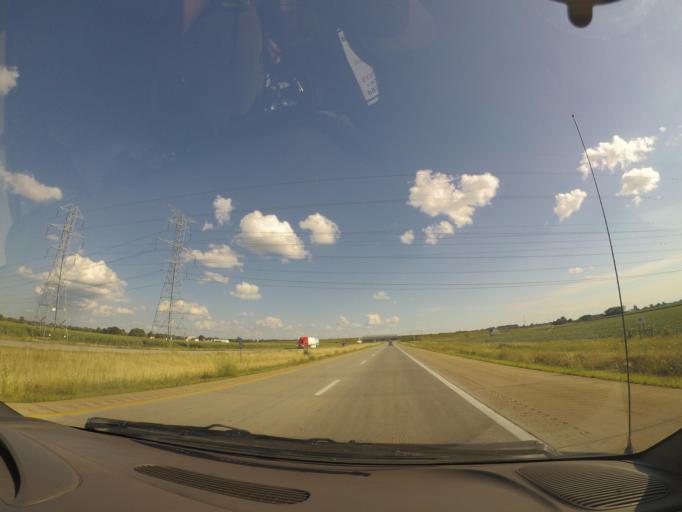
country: US
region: Ohio
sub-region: Lucas County
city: Whitehouse
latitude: 41.4778
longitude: -83.7767
